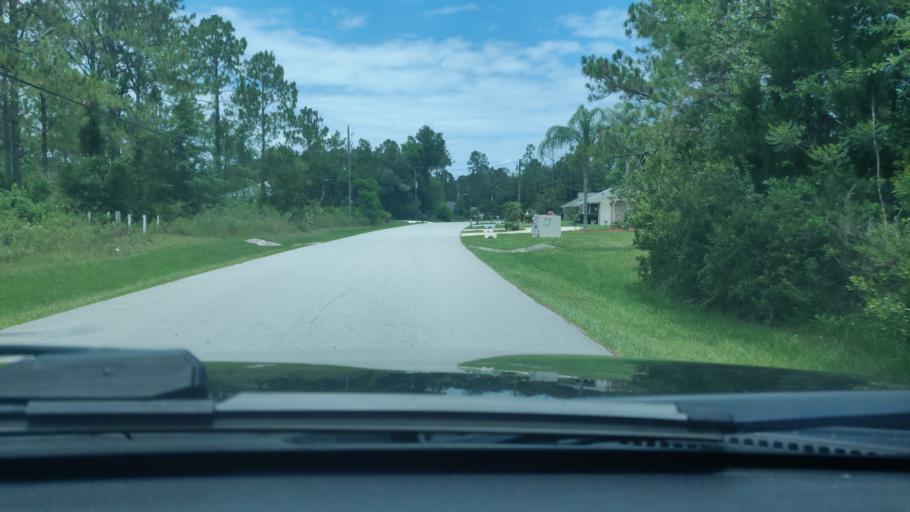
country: US
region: Florida
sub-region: Flagler County
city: Bunnell
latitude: 29.5237
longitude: -81.2409
